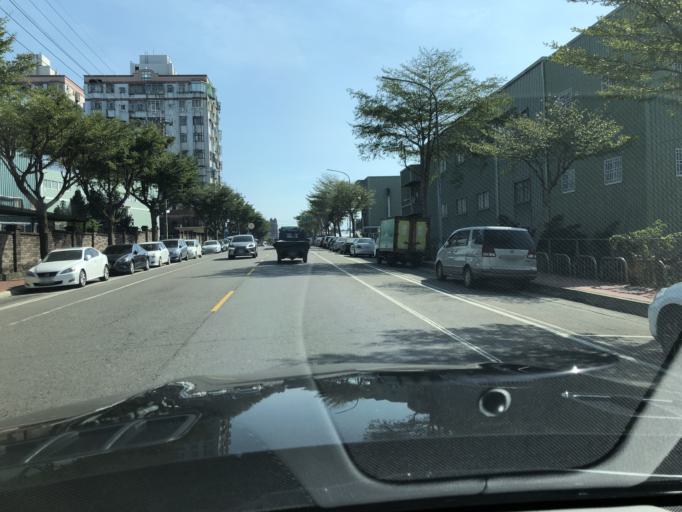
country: TW
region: Taiwan
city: Taoyuan City
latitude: 25.0679
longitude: 121.2899
